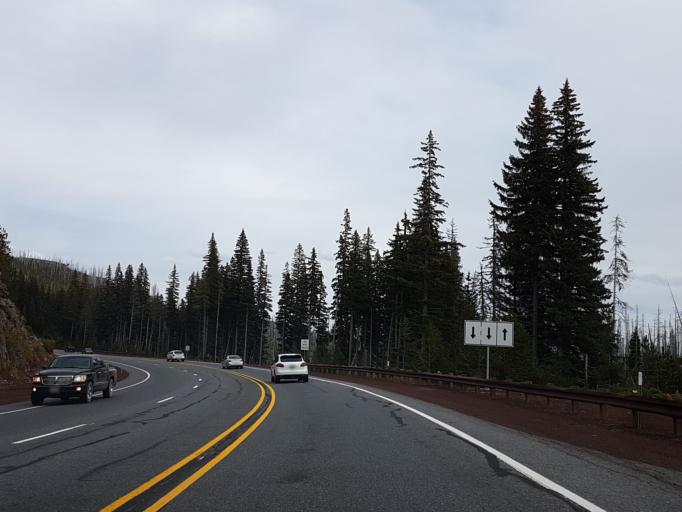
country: US
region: Oregon
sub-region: Deschutes County
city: Sisters
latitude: 44.4233
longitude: -121.8277
